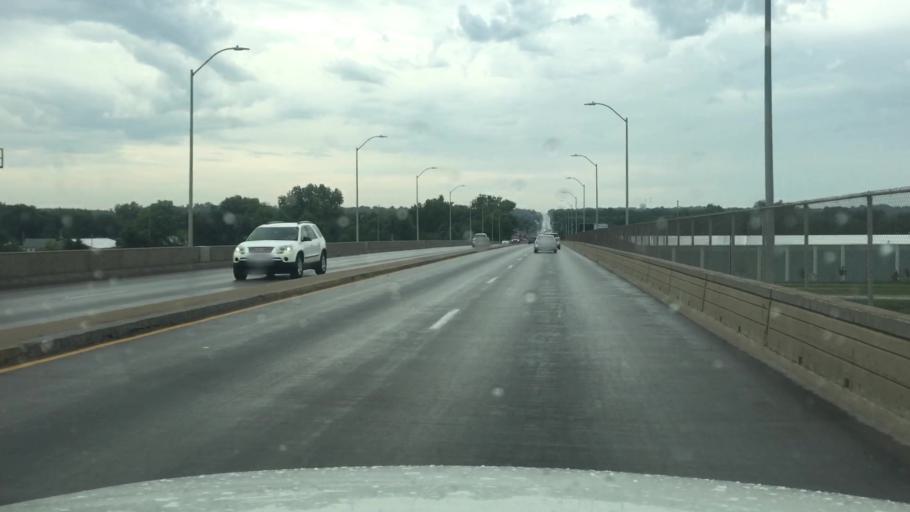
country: US
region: Iowa
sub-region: Polk County
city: Des Moines
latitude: 41.5863
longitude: -93.5969
